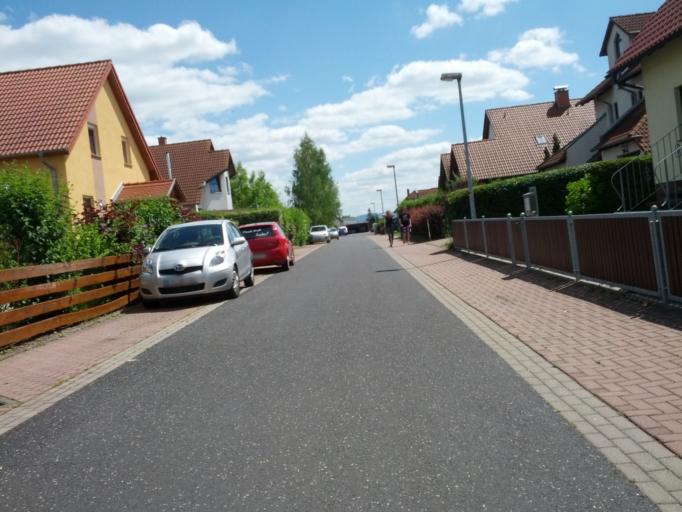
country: DE
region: Thuringia
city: Bischofroda
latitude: 51.0189
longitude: 10.3368
